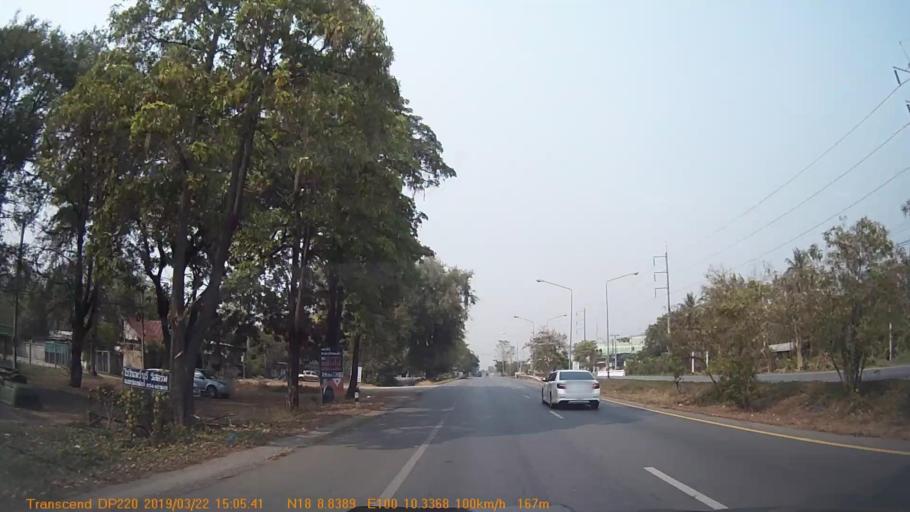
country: TH
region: Phrae
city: Phrae
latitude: 18.1475
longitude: 100.1724
